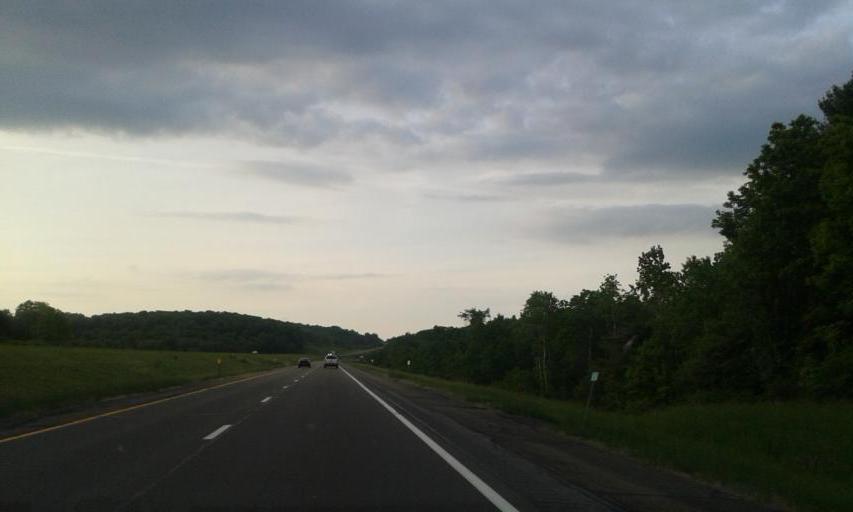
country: US
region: New York
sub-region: Broome County
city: Chenango Bridge
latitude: 42.2449
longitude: -75.9171
